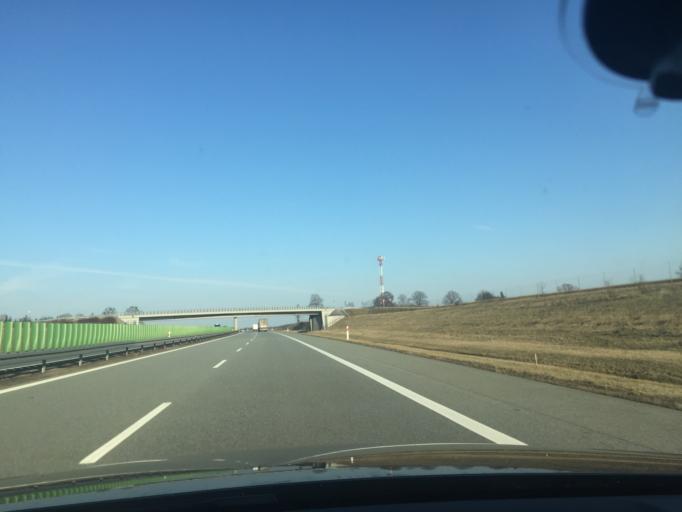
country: PL
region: Greater Poland Voivodeship
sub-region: Powiat nowotomyski
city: Lwowek
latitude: 52.3691
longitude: 16.2048
